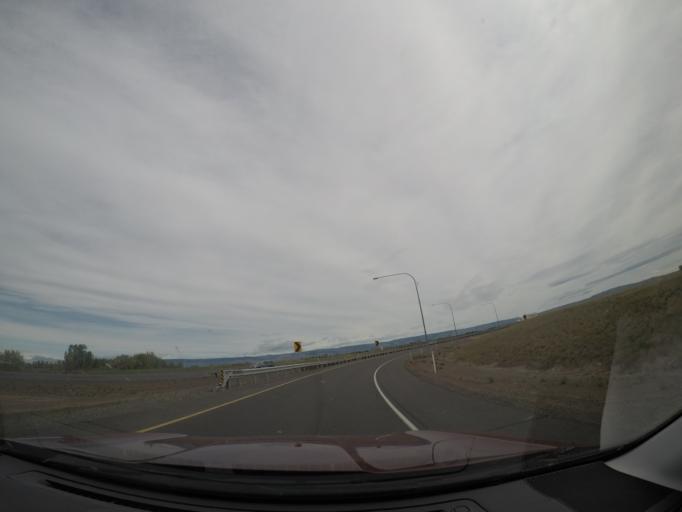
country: US
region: Washington
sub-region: Kittitas County
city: Ellensburg
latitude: 46.9719
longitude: -120.5173
